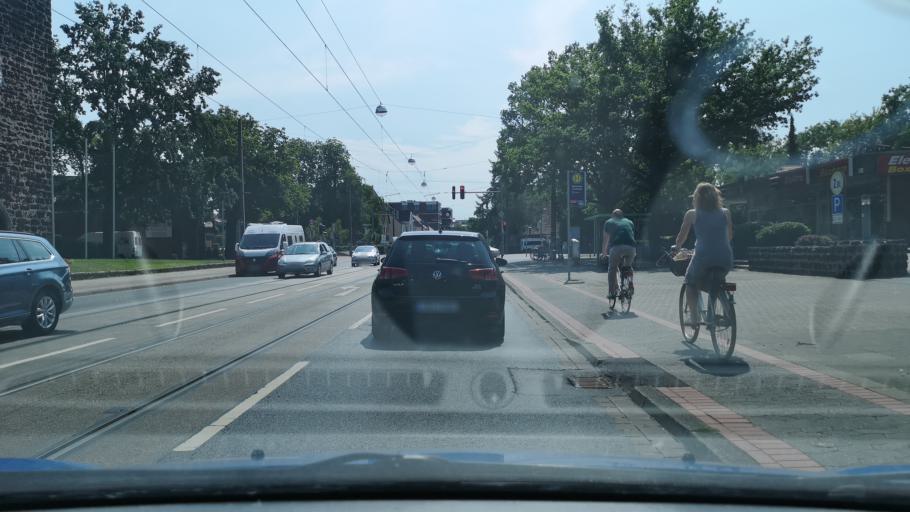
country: DE
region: Lower Saxony
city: Langenhagen
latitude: 52.4132
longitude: 9.7979
